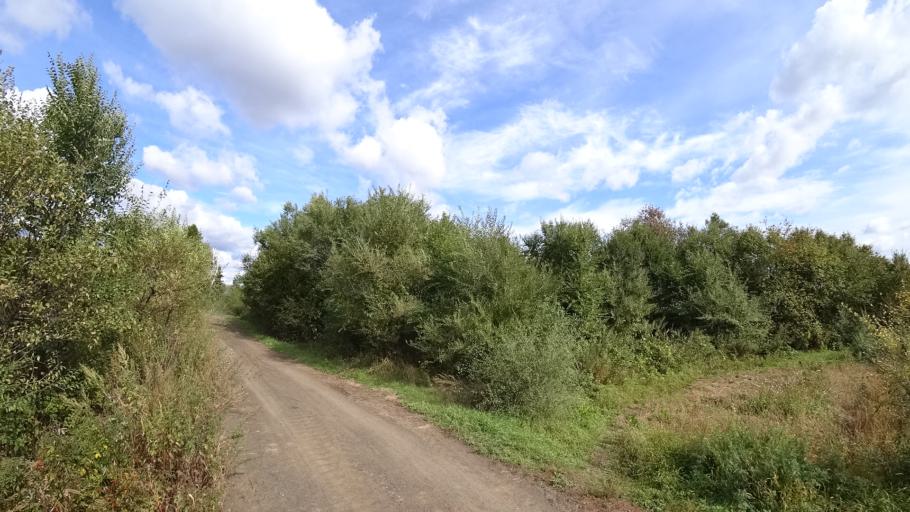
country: RU
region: Amur
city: Arkhara
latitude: 49.3514
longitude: 130.1600
